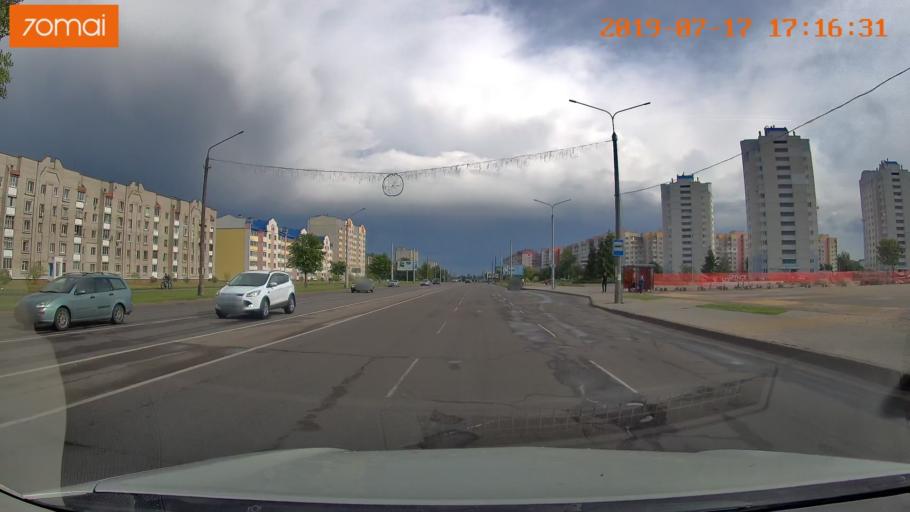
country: BY
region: Mogilev
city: Babruysk
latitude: 53.1675
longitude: 29.1935
